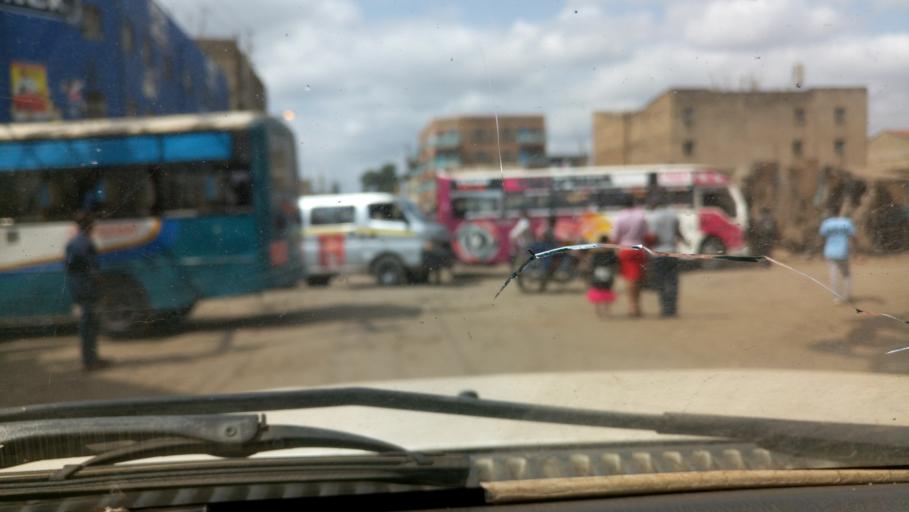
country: KE
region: Nairobi Area
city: Pumwani
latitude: -1.2843
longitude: 36.8555
